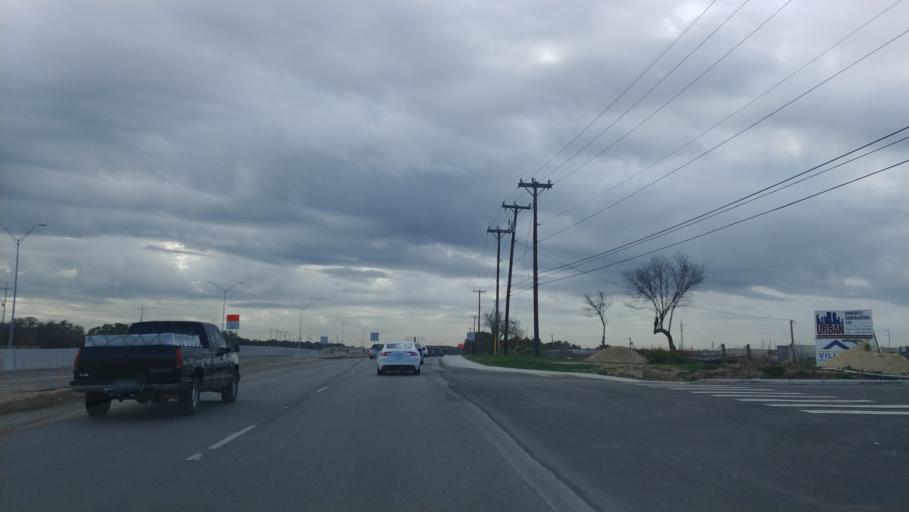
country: US
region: Texas
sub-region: Bexar County
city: Lackland Air Force Base
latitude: 29.4312
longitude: -98.7118
